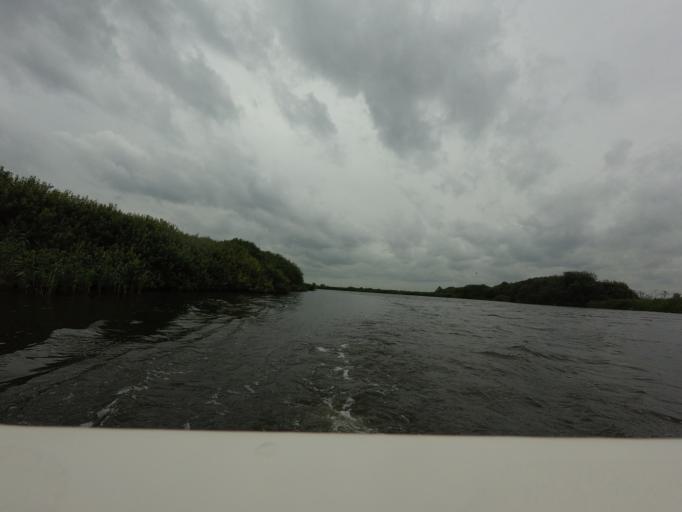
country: NL
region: Friesland
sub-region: Gemeente Boarnsterhim
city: Warten
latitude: 53.1011
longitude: 5.9067
